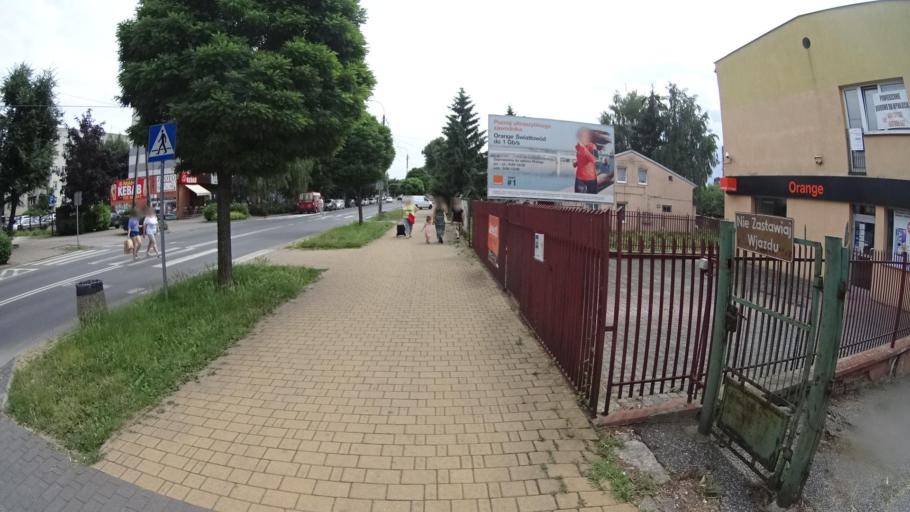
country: PL
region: Masovian Voivodeship
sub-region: Powiat grojecki
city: Grojec
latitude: 51.8637
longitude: 20.8673
